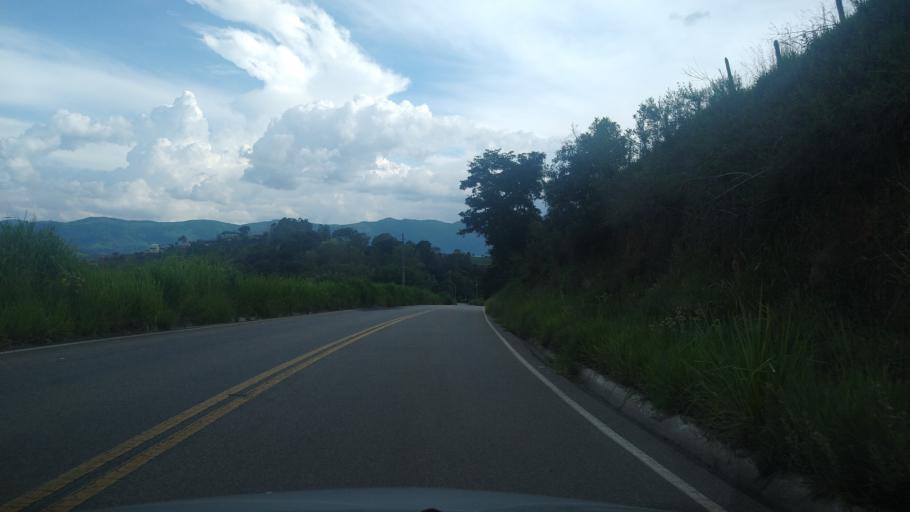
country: BR
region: Minas Gerais
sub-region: Extrema
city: Extrema
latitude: -22.7882
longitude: -46.3192
